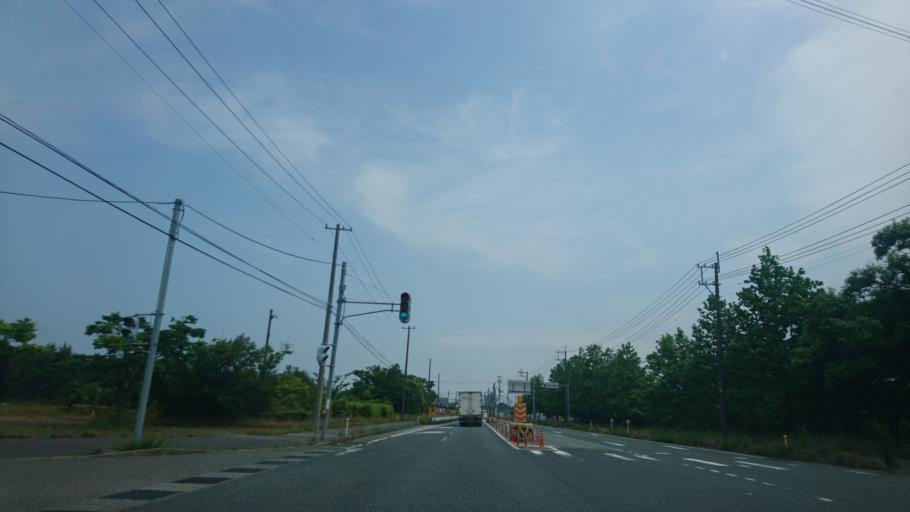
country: JP
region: Niigata
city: Shibata
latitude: 37.9976
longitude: 139.2550
